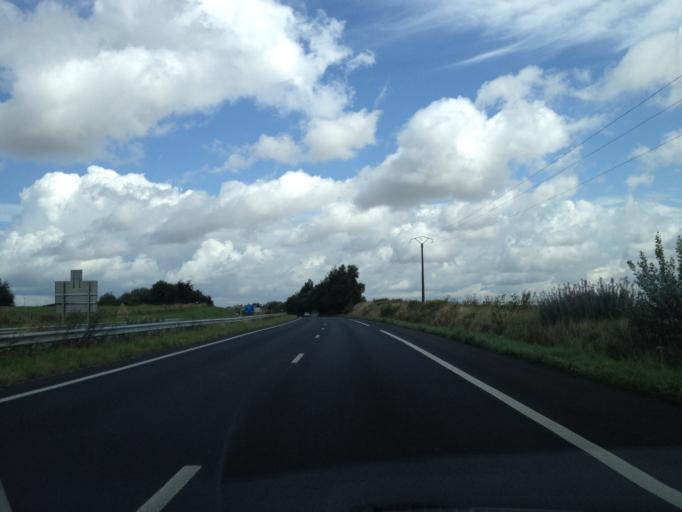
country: FR
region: Haute-Normandie
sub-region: Departement de la Seine-Maritime
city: Blainville-Crevon
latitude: 49.5653
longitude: 1.2728
